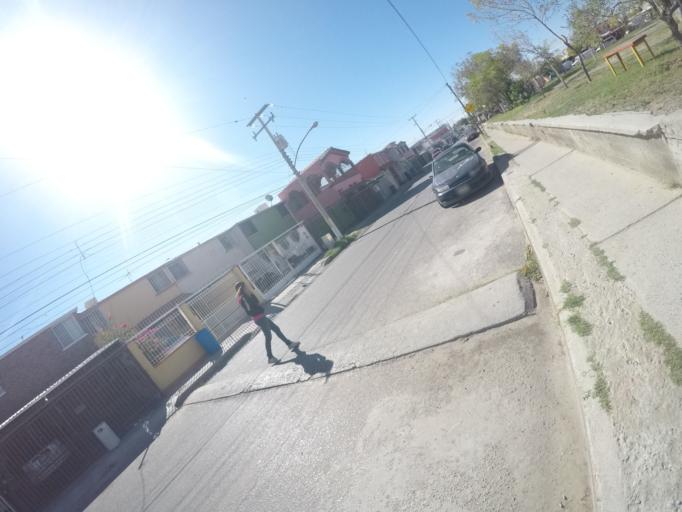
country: US
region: Texas
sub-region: El Paso County
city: Socorro
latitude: 31.6683
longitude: -106.4045
